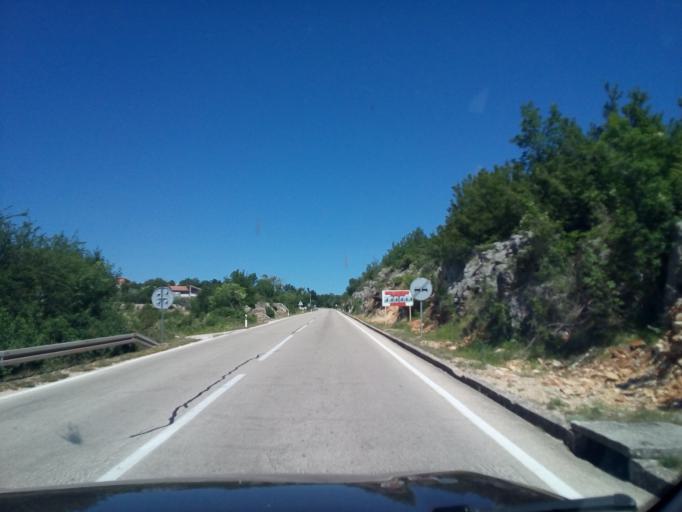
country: HR
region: Zadarska
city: Krusevo
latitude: 44.1829
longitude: 15.6238
